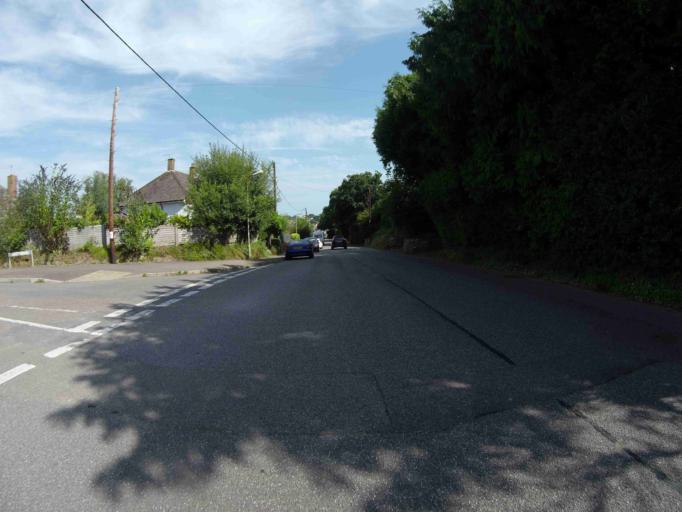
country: GB
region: England
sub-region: Devon
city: Budleigh Salterton
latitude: 50.6365
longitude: -3.3358
